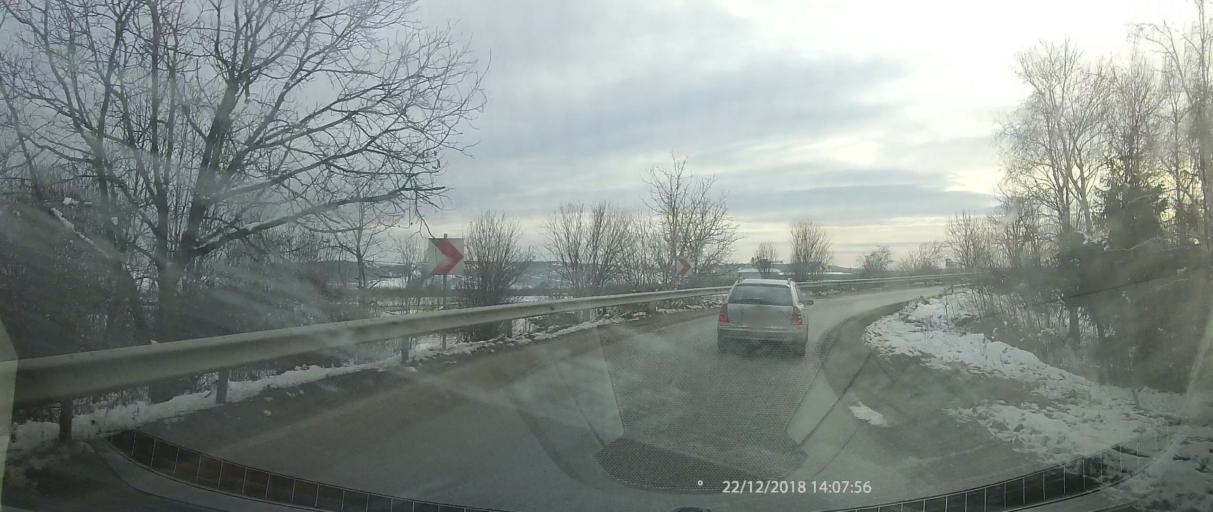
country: BG
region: Pleven
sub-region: Obshtina Dolna Mitropoliya
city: Dolna Mitropoliya
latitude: 43.4250
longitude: 24.5021
